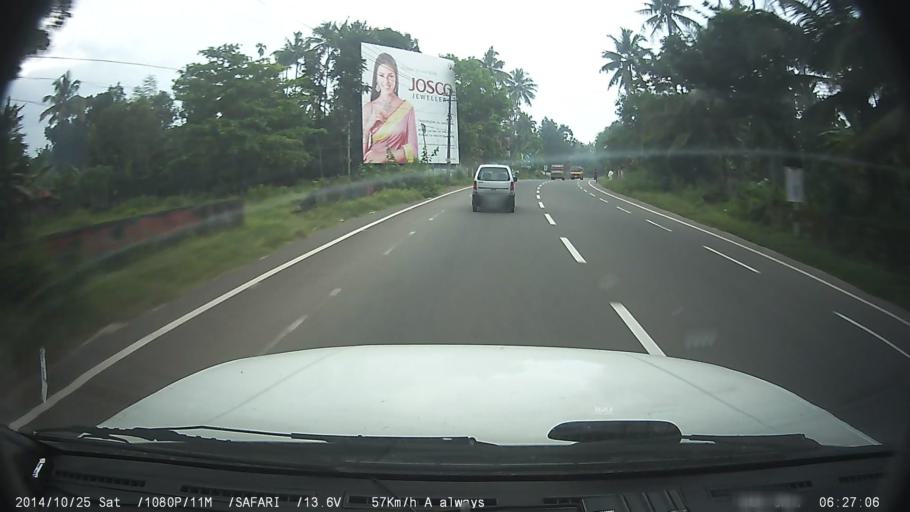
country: IN
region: Kerala
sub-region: Ernakulam
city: Perumbavoor
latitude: 10.0576
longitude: 76.5288
